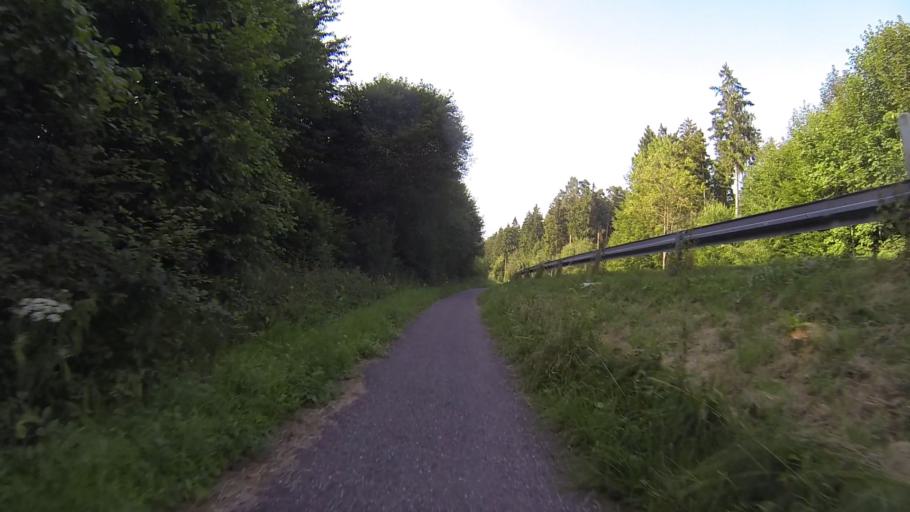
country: DE
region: Baden-Wuerttemberg
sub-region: Tuebingen Region
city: Staig
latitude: 48.3122
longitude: 9.9680
